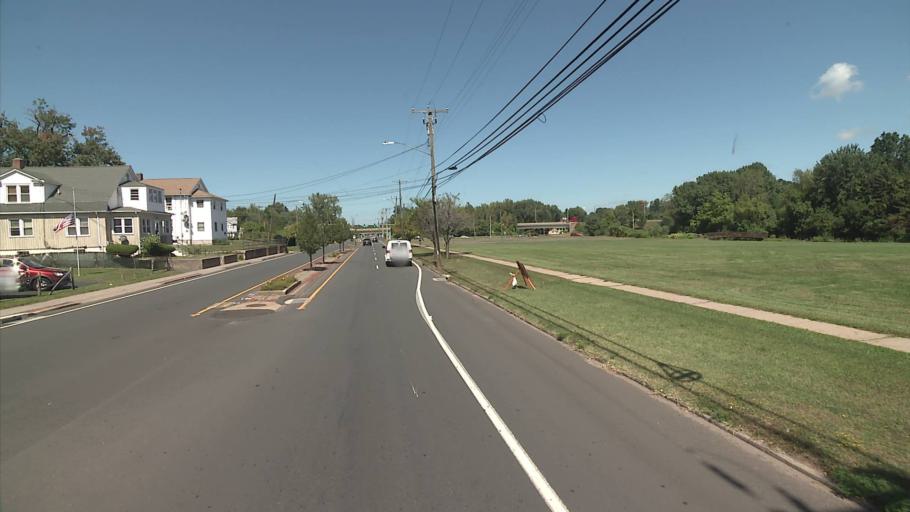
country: US
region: Connecticut
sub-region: Hartford County
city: South Windsor
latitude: 41.8153
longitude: -72.6570
